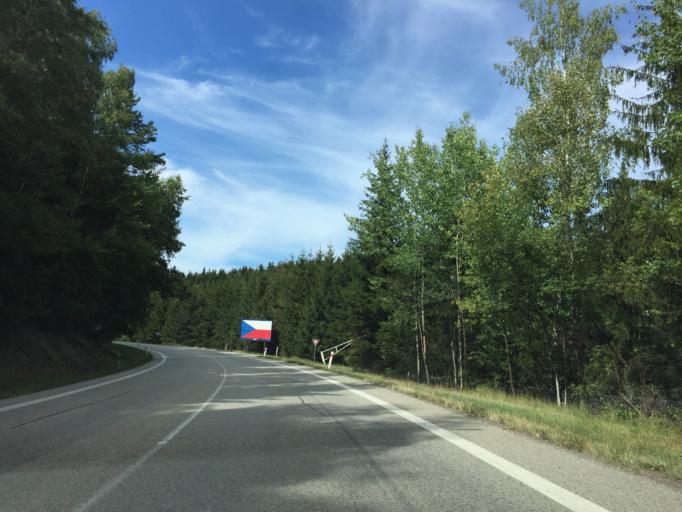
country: CZ
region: Central Bohemia
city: Votice
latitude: 49.5853
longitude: 14.6635
